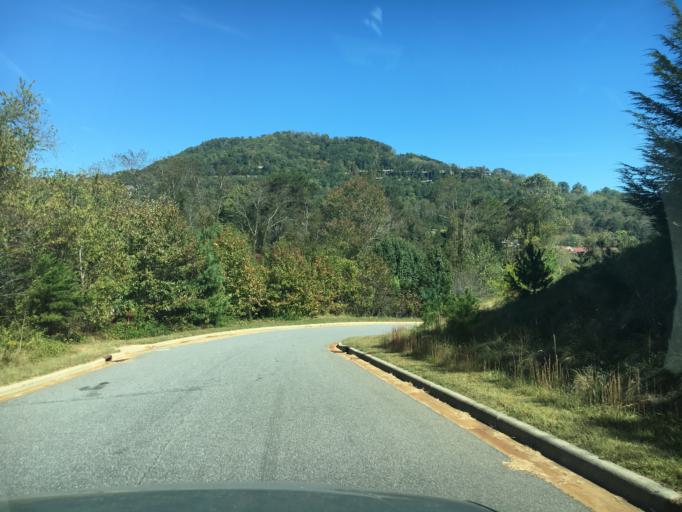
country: US
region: North Carolina
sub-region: Buncombe County
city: Woodfin
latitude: 35.6458
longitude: -82.5848
